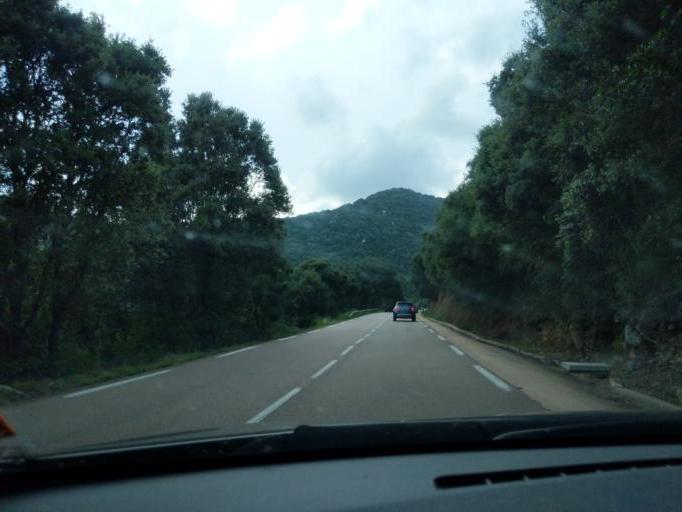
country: FR
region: Corsica
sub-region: Departement de la Corse-du-Sud
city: Sartene
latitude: 41.5782
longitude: 8.9523
